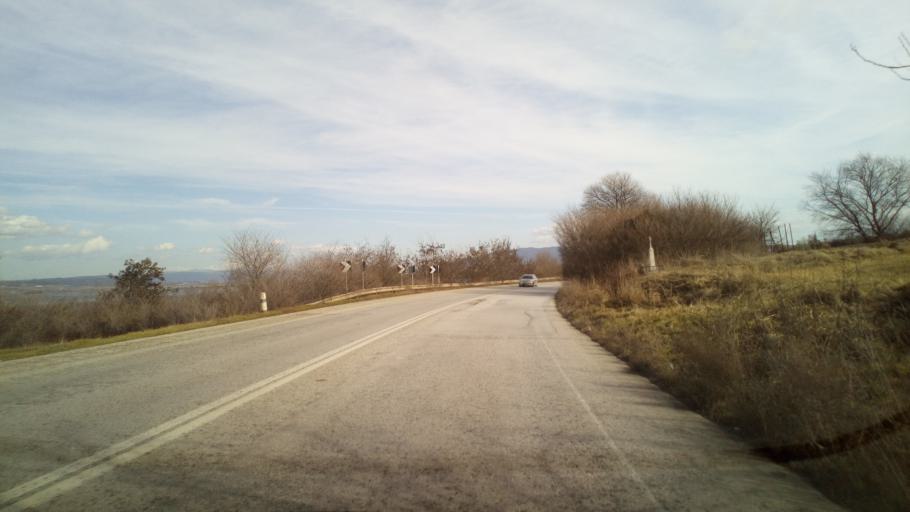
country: GR
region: Central Macedonia
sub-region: Nomos Thessalonikis
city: Agios Vasileios
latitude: 40.6564
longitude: 23.1522
